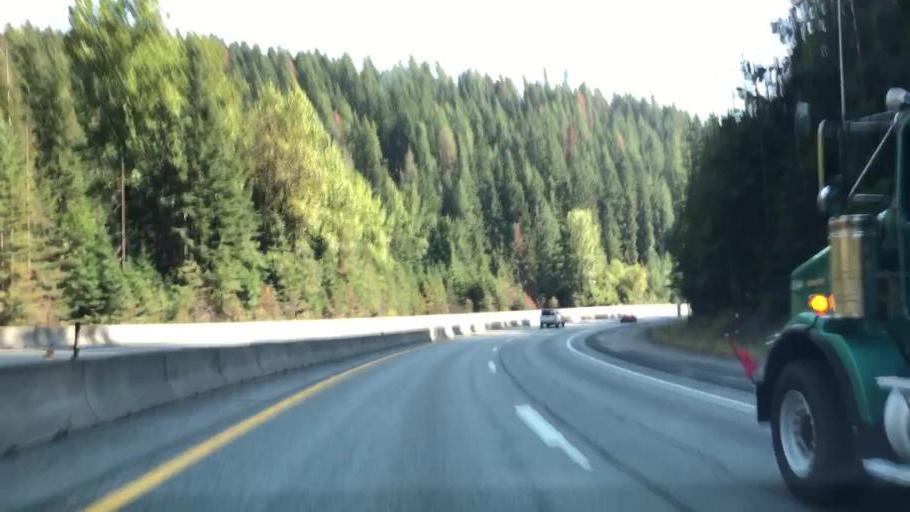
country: US
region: Idaho
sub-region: Shoshone County
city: Pinehurst
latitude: 47.5971
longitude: -116.4929
